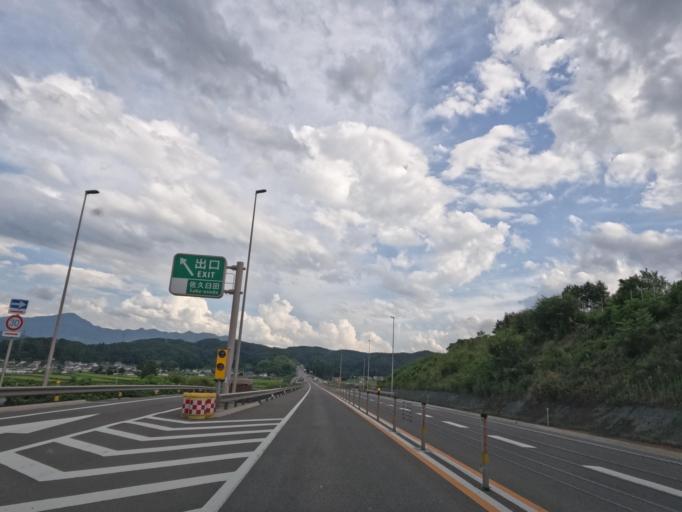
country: JP
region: Nagano
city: Saku
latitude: 36.1885
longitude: 138.4692
